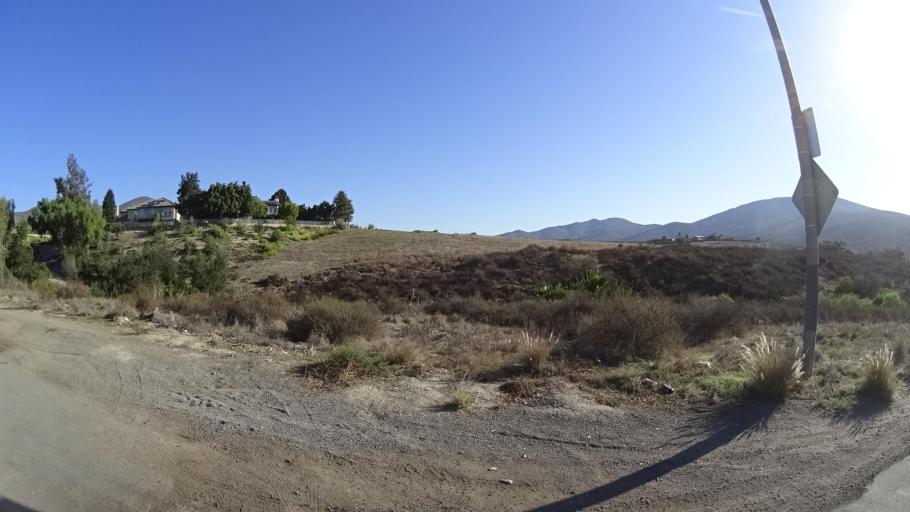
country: US
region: California
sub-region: San Diego County
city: La Presa
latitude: 32.6595
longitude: -116.9411
